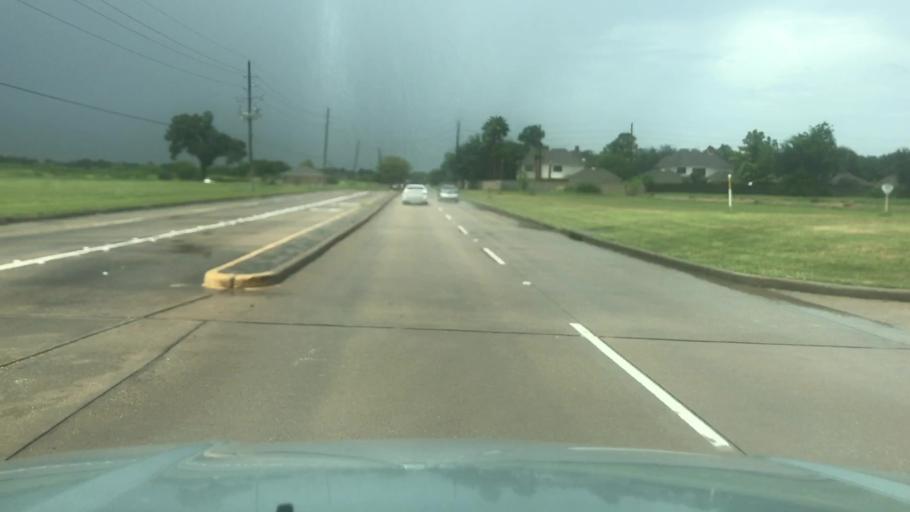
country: US
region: Texas
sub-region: Harris County
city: Katy
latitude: 29.7593
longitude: -95.8090
